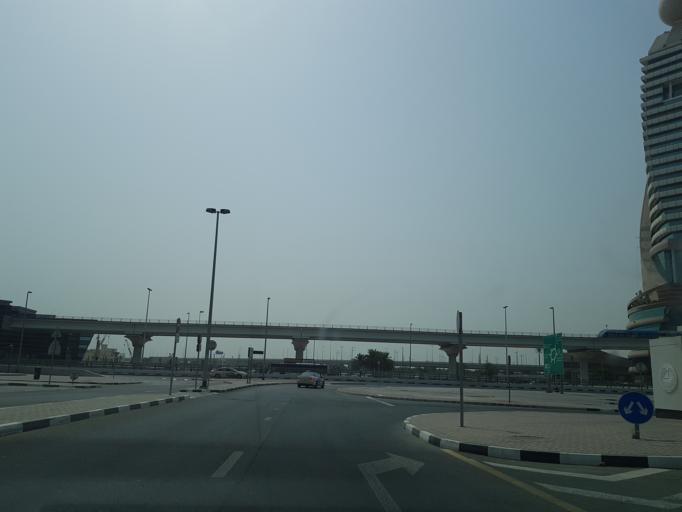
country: AE
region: Ash Shariqah
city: Sharjah
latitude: 25.2330
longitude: 55.2905
